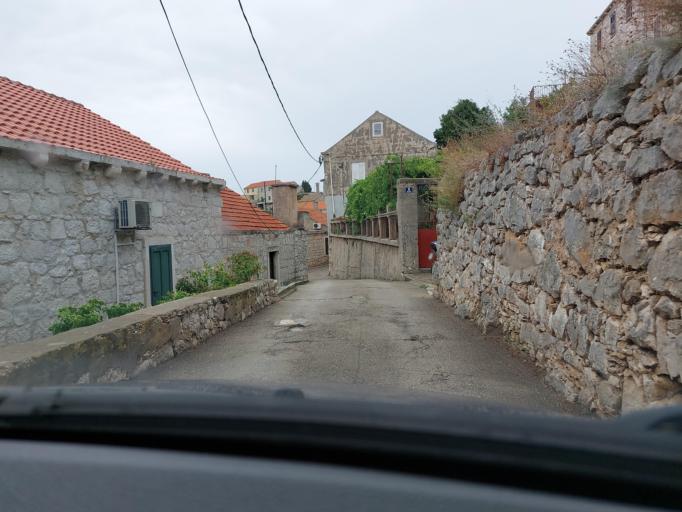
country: HR
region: Dubrovacko-Neretvanska
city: Smokvica
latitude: 42.7673
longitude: 16.8982
